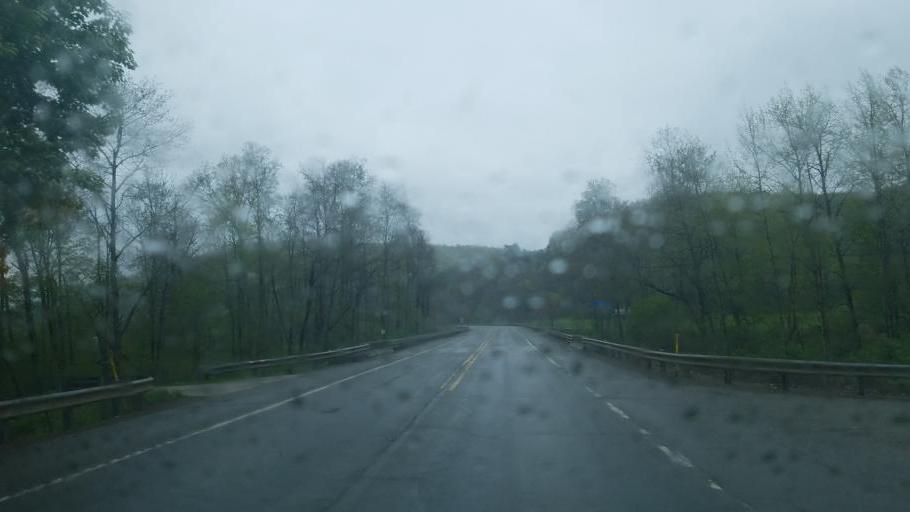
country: US
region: Pennsylvania
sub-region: Potter County
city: Coudersport
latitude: 41.7735
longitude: -78.1298
